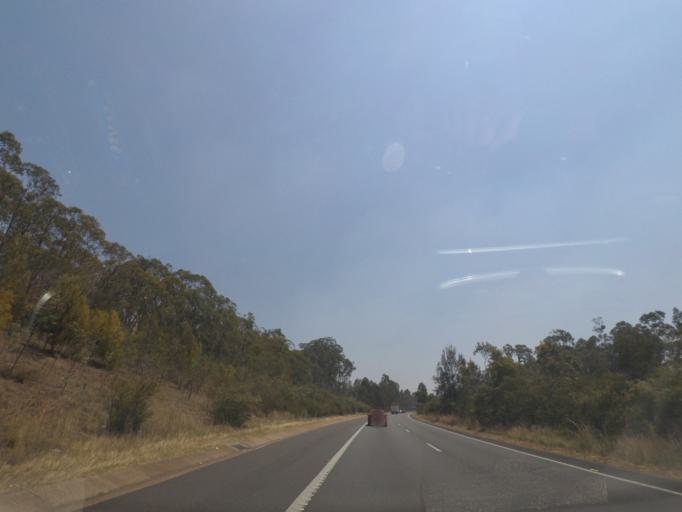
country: AU
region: New South Wales
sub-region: Newcastle
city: Beresfield
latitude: -32.8306
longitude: 151.6337
